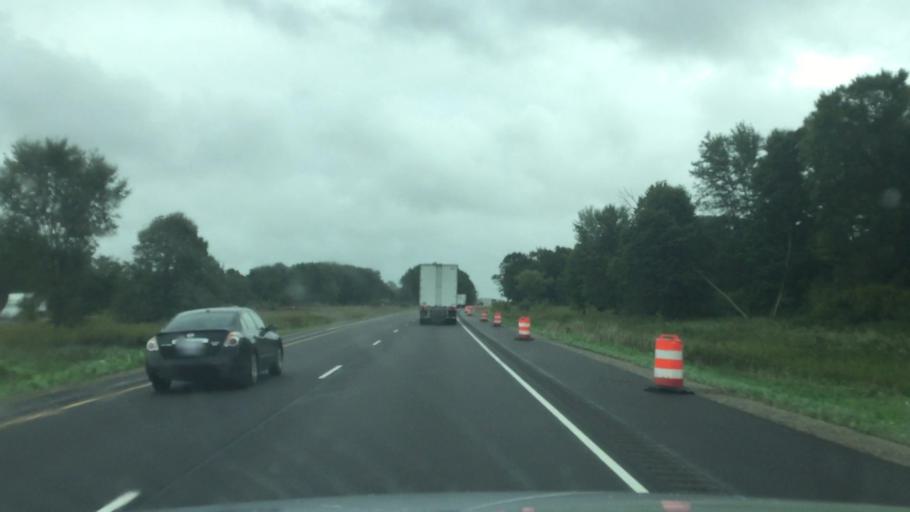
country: US
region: Michigan
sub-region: Livingston County
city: Fowlerville
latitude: 42.6393
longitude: -84.0337
